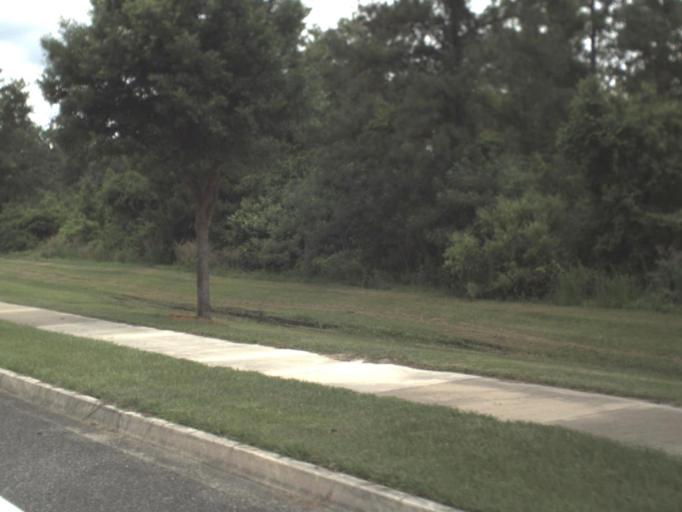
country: US
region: Florida
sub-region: Duval County
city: Jacksonville
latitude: 30.4747
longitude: -81.6674
